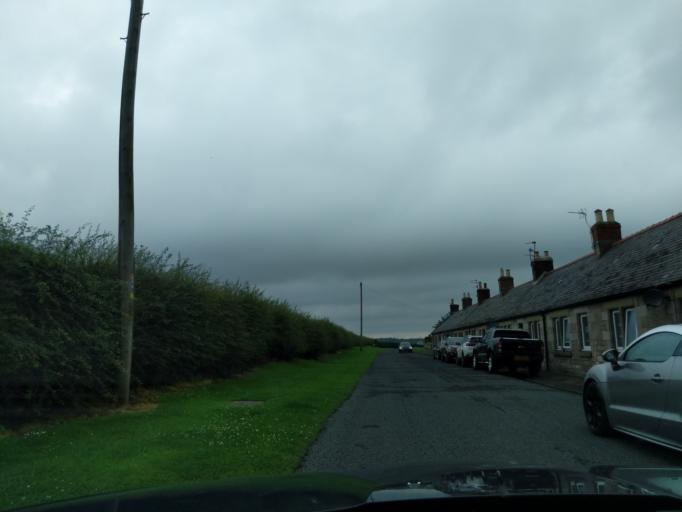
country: GB
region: England
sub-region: Northumberland
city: Ford
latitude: 55.6967
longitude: -2.1380
